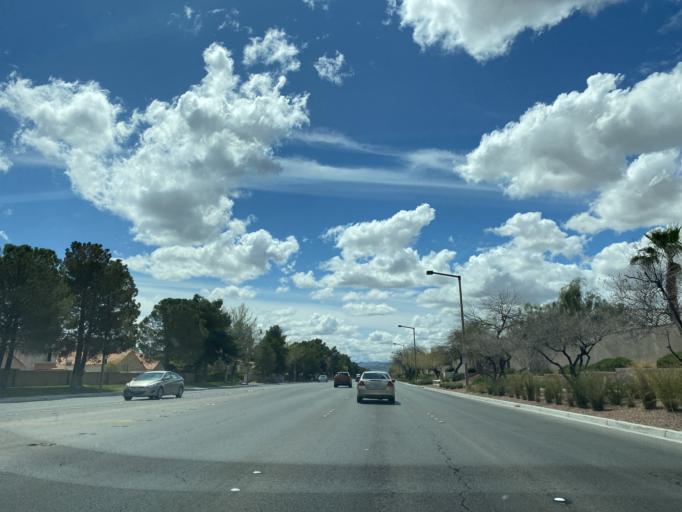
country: US
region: Nevada
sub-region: Clark County
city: Summerlin South
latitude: 36.1427
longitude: -115.3155
